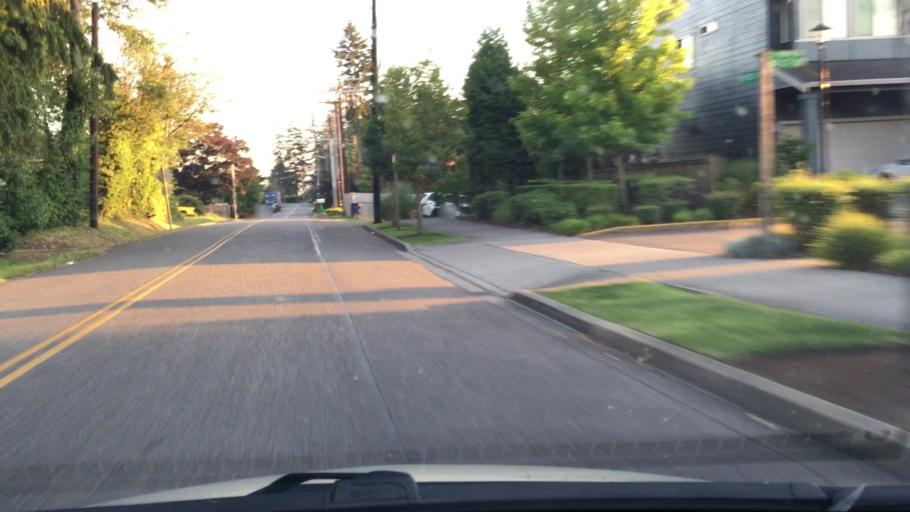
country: US
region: Washington
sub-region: Snohomish County
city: Martha Lake
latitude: 47.8536
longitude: -122.2524
